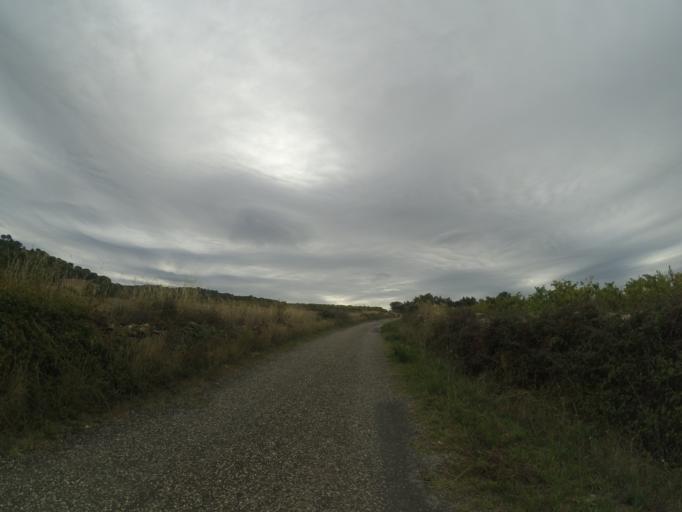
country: FR
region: Languedoc-Roussillon
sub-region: Departement des Pyrenees-Orientales
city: Estagel
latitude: 42.7650
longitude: 2.6926
